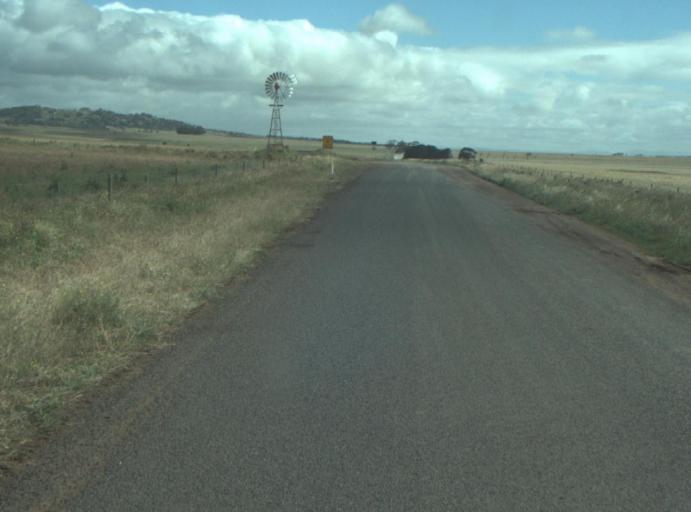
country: AU
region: Victoria
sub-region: Greater Geelong
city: Lara
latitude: -37.9166
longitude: 144.3142
